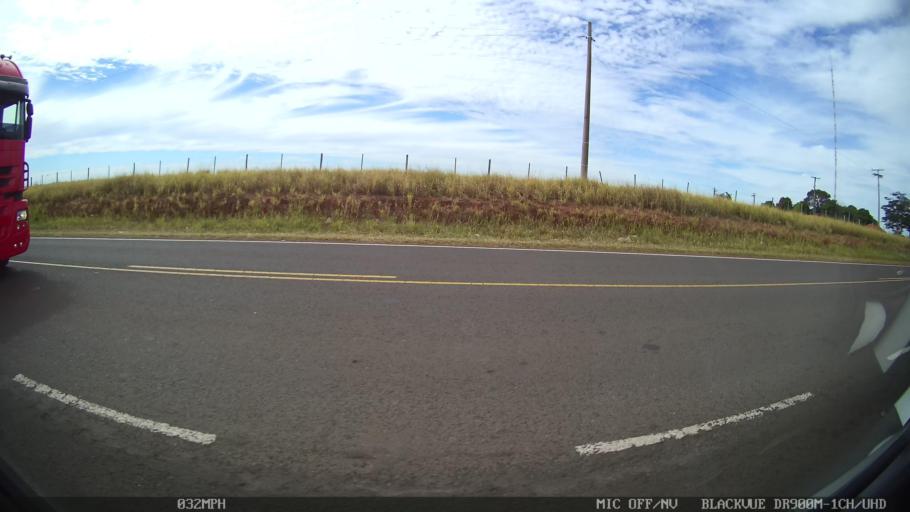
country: BR
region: Sao Paulo
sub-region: Catanduva
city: Catanduva
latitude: -21.1624
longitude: -48.9629
